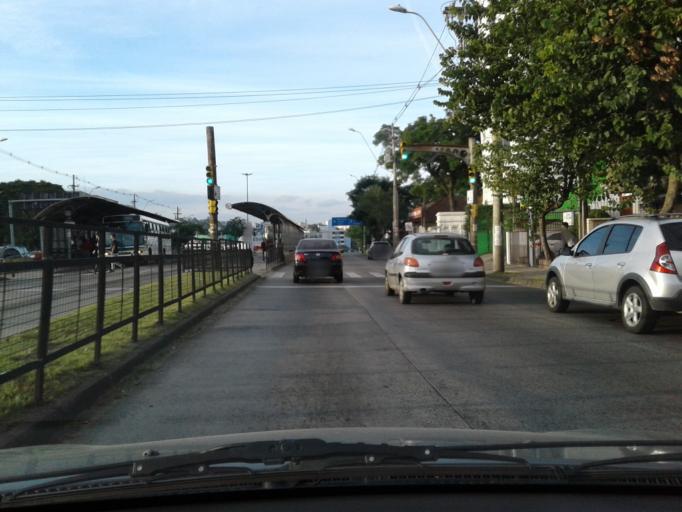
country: BR
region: Rio Grande do Sul
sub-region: Porto Alegre
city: Porto Alegre
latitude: -30.0793
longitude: -51.2091
